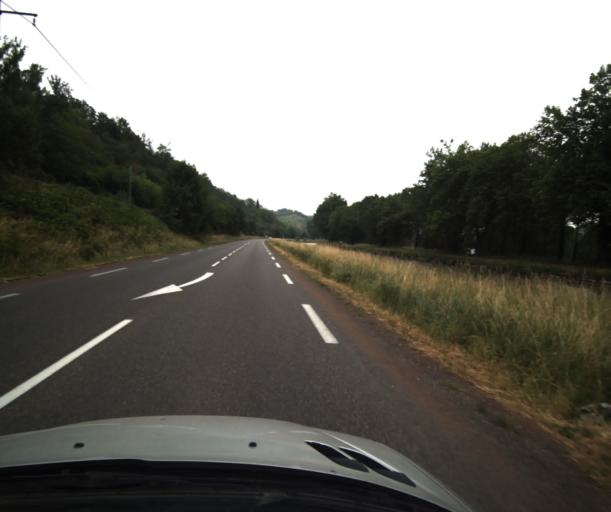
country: FR
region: Midi-Pyrenees
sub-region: Departement du Tarn-et-Garonne
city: Moissac
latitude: 44.0978
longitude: 1.0653
